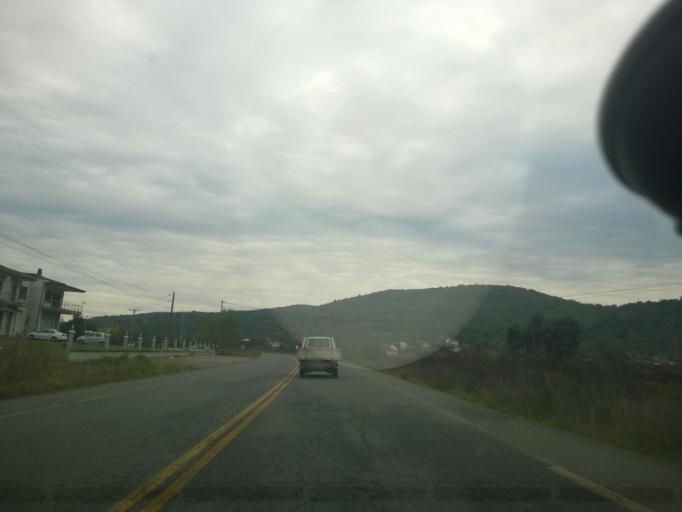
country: GR
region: Central Macedonia
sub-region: Nomos Pellis
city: Apsalos
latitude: 40.8935
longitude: 22.0629
